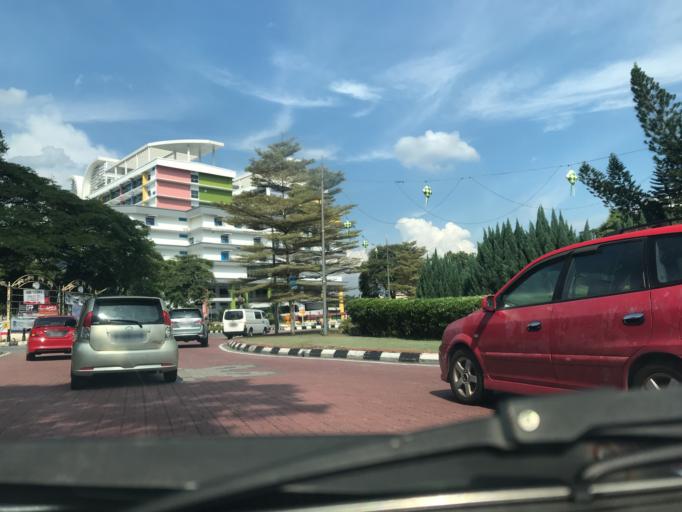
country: MY
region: Perak
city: Ipoh
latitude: 4.6040
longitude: 101.0865
